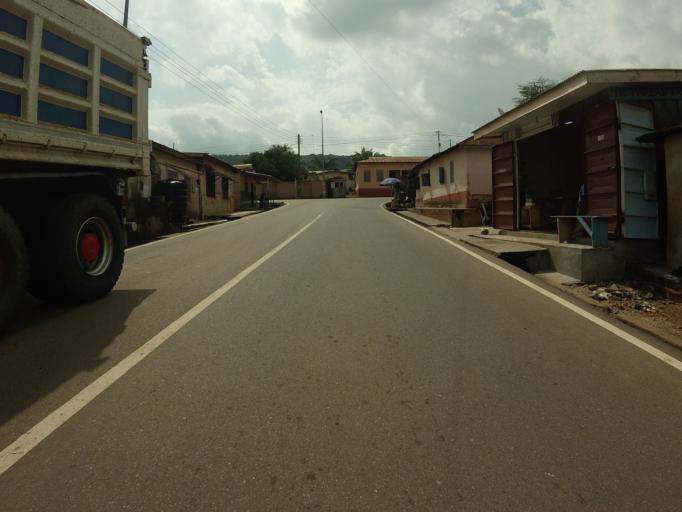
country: GH
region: Volta
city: Ho
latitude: 6.6176
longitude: 0.4656
